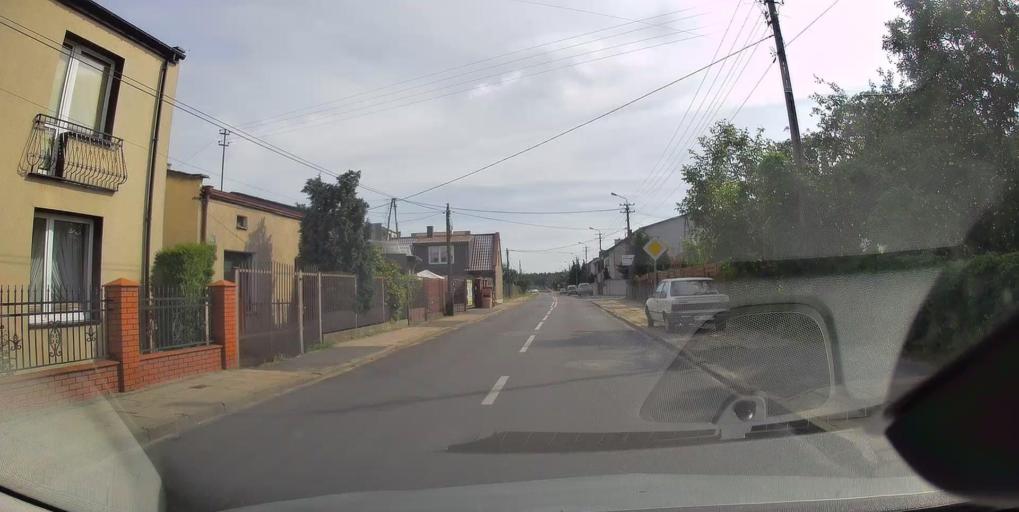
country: PL
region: Lodz Voivodeship
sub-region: Powiat tomaszowski
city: Tomaszow Mazowiecki
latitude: 51.5240
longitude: 19.9976
